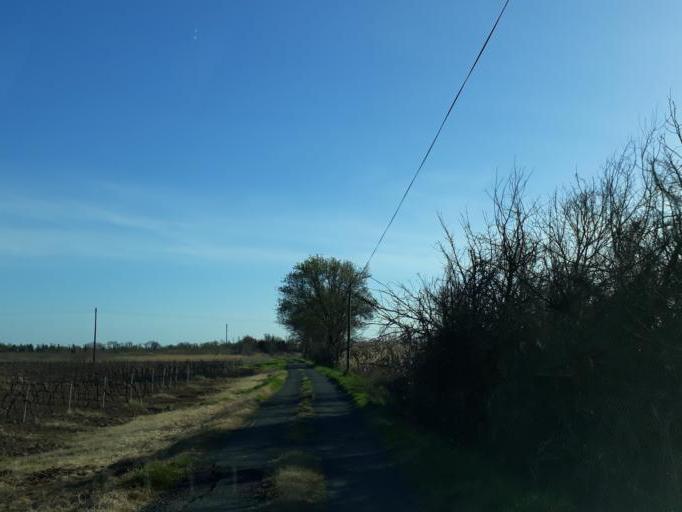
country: FR
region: Languedoc-Roussillon
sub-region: Departement de l'Herault
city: Agde
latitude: 43.3257
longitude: 3.4525
